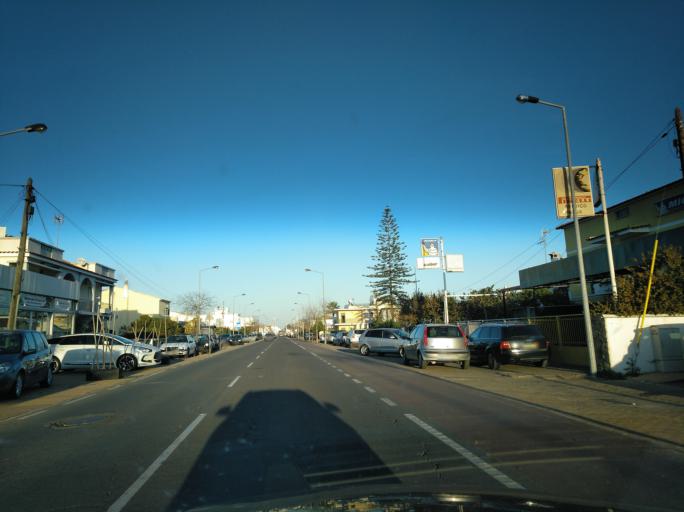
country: PT
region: Faro
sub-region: Vila Real de Santo Antonio
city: Vila Real de Santo Antonio
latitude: 37.1907
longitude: -7.4345
